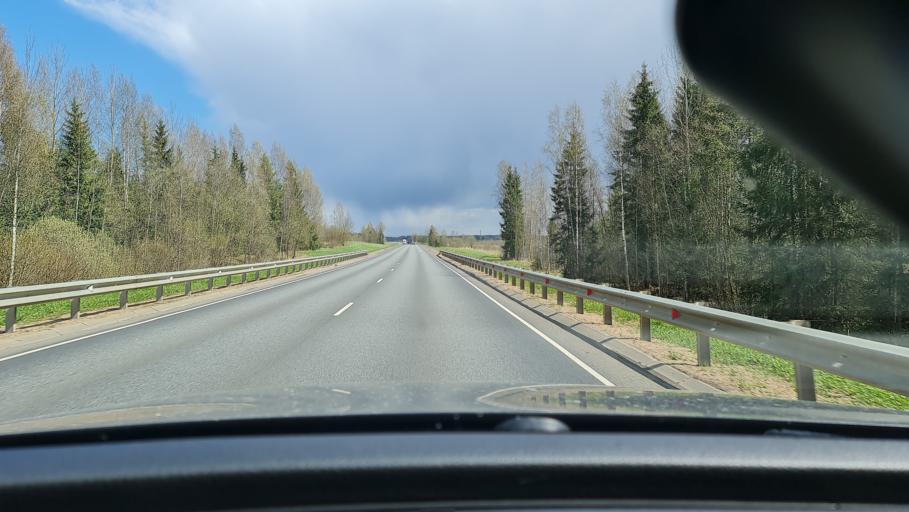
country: RU
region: Tverskaya
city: Zapadnaya Dvina
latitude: 56.3025
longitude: 32.3935
